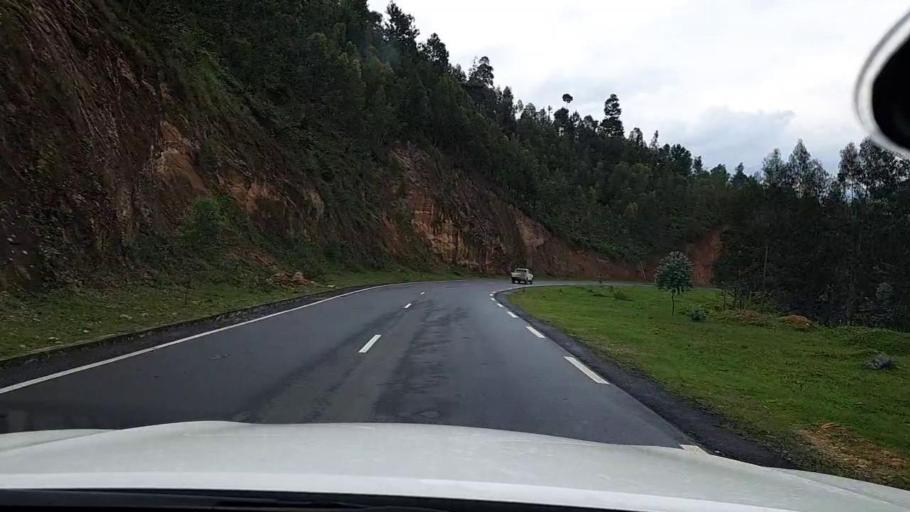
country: RW
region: Western Province
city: Kibuye
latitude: -2.1601
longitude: 29.2959
